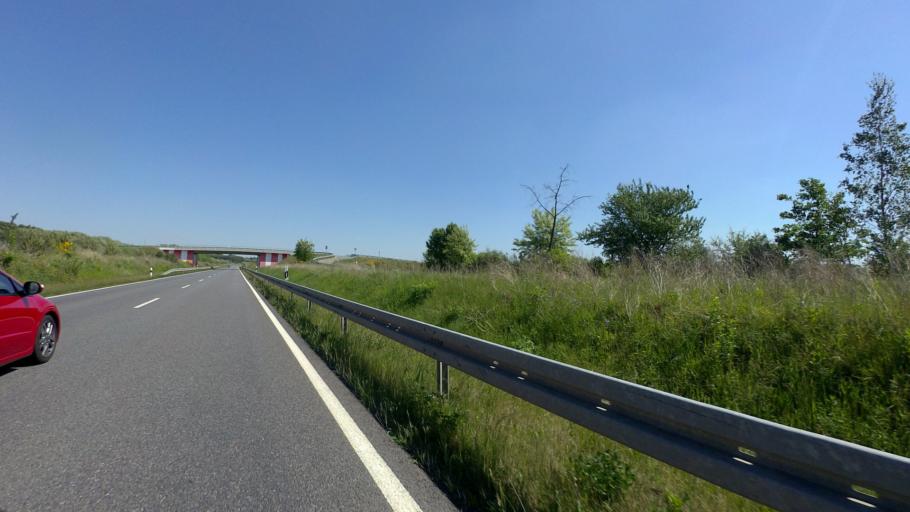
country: DE
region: Brandenburg
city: Spremberg
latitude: 51.5686
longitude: 14.3326
